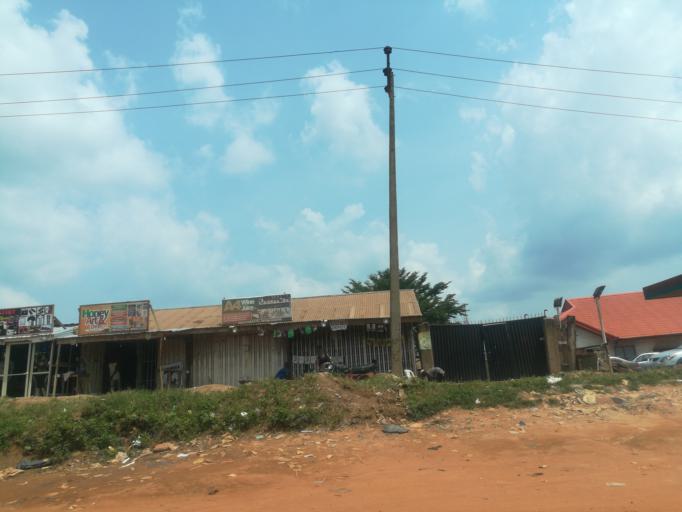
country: NG
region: Oyo
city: Ibadan
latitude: 7.4488
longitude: 3.9510
